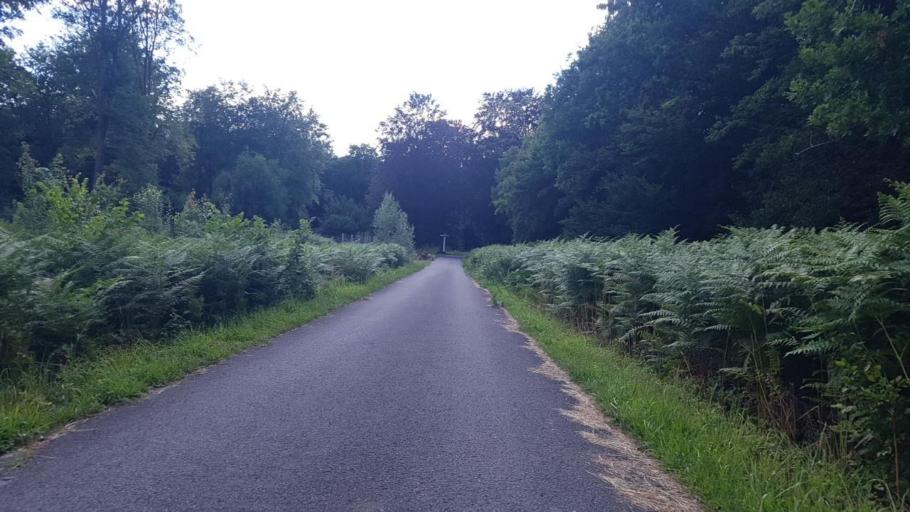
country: FR
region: Picardie
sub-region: Departement de l'Oise
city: Ver-sur-Launette
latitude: 49.1136
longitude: 2.6656
